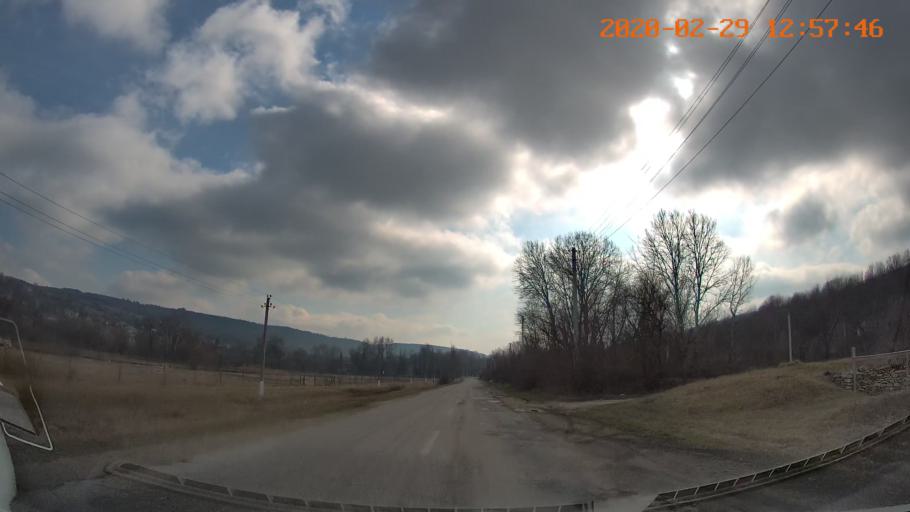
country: MD
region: Telenesti
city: Camenca
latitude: 48.0749
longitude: 28.7168
